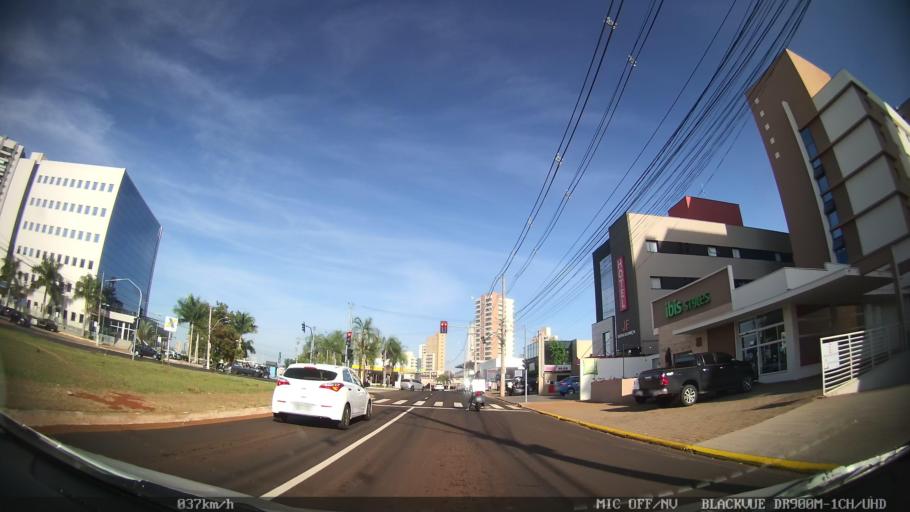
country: BR
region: Sao Paulo
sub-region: Ribeirao Preto
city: Ribeirao Preto
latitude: -21.2166
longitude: -47.8244
